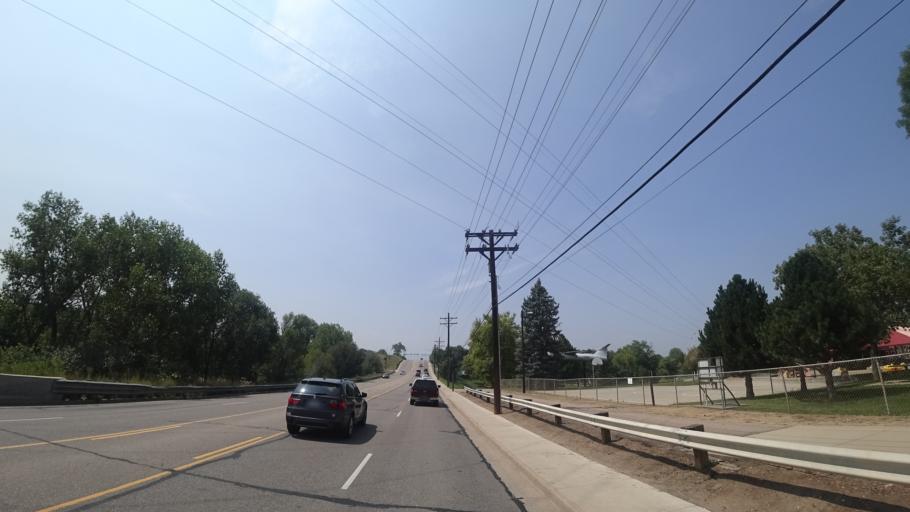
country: US
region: Colorado
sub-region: Arapahoe County
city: Littleton
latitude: 39.6241
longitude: -104.9987
